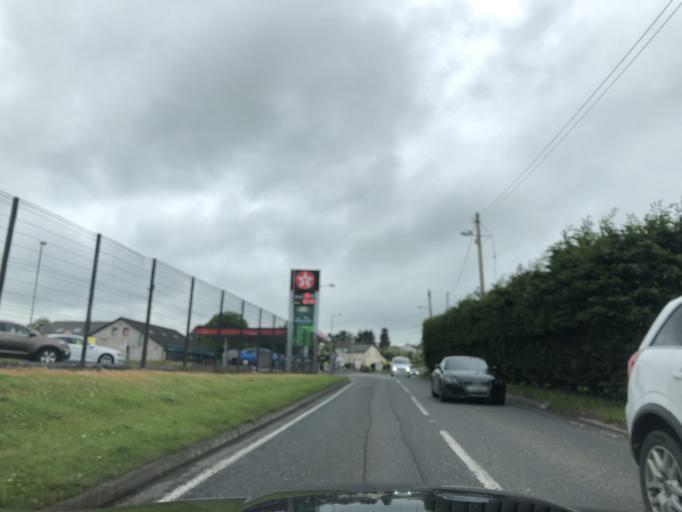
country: GB
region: Northern Ireland
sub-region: Lisburn District
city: Lisburn
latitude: 54.5477
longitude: -6.0753
